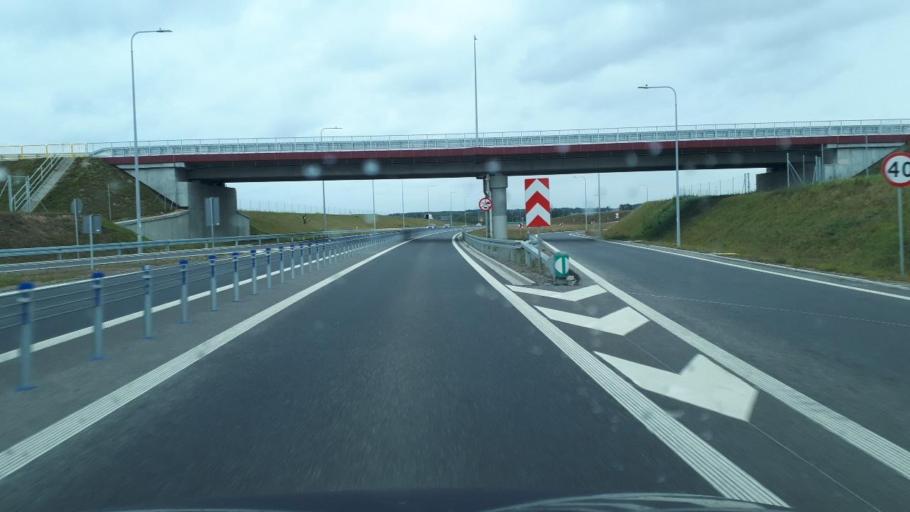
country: PL
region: Greater Poland Voivodeship
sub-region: Powiat kepinski
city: Baranow
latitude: 51.2555
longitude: 18.0154
